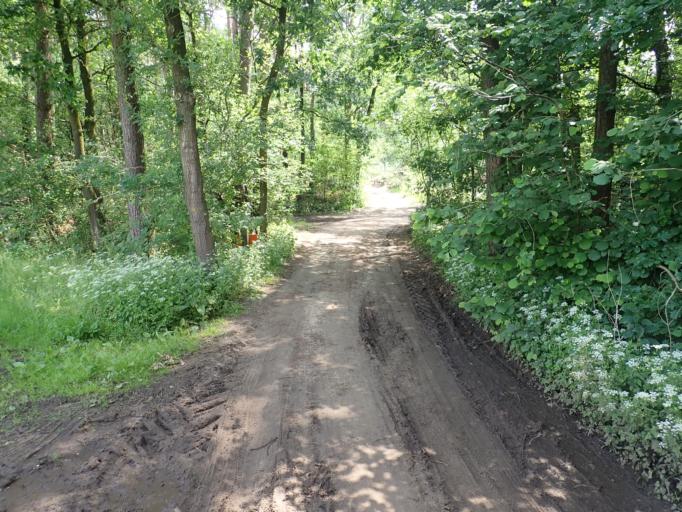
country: BE
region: Flanders
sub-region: Provincie Antwerpen
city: Herentals
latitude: 51.2158
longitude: 4.8804
